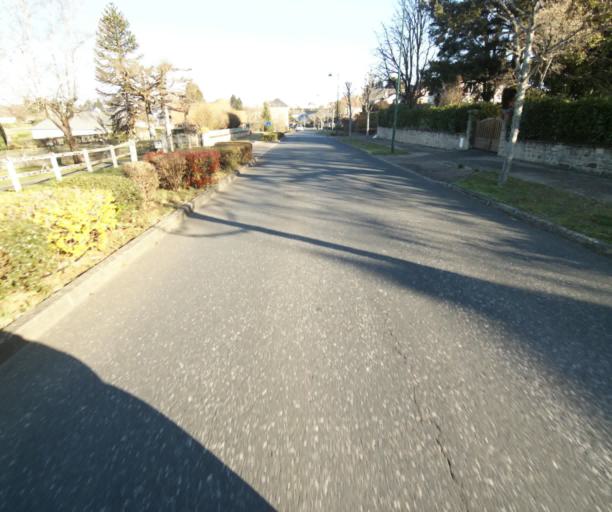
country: FR
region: Limousin
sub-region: Departement de la Correze
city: Seilhac
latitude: 45.3635
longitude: 1.7243
